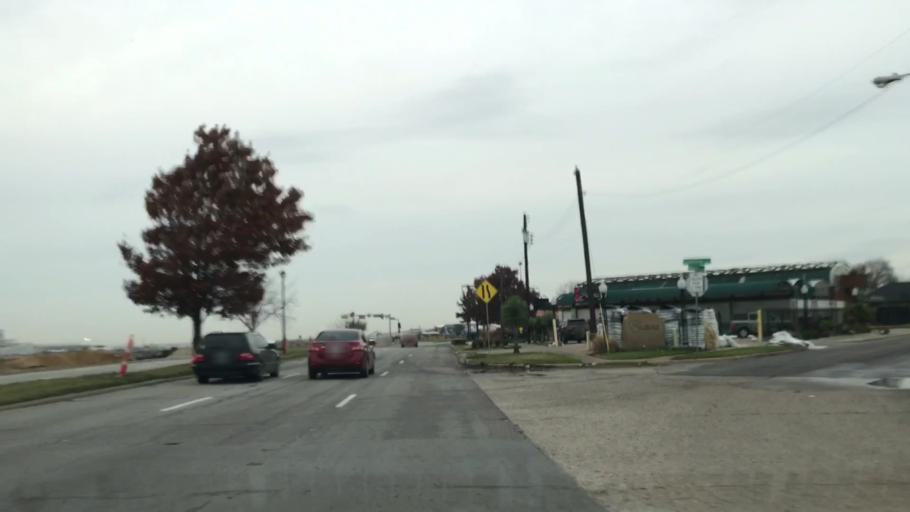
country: US
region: Texas
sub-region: Dallas County
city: University Park
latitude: 32.8383
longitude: -96.8333
